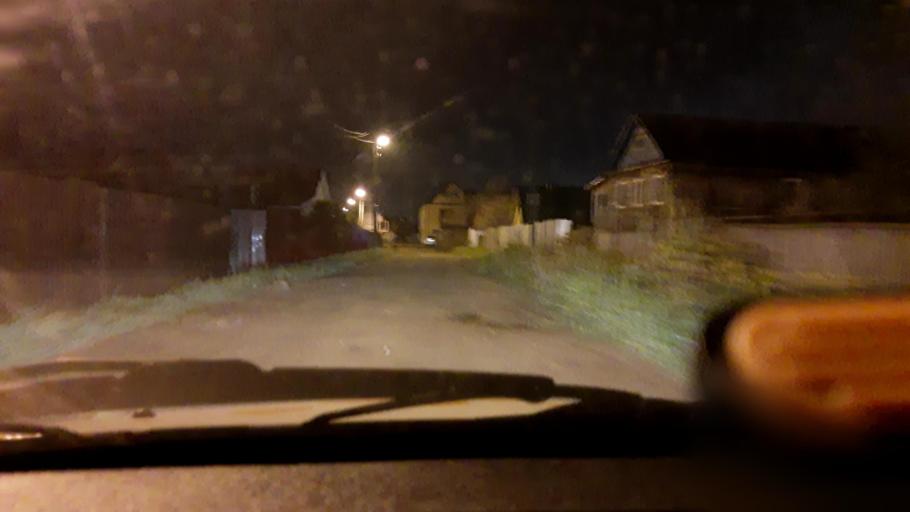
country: RU
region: Bashkortostan
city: Mikhaylovka
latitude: 54.7465
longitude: 55.9003
